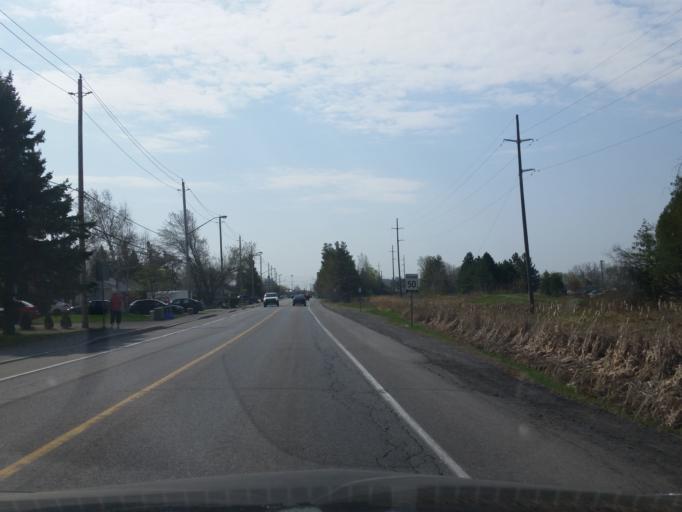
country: CA
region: Ontario
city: Ottawa
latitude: 45.4393
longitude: -75.6113
